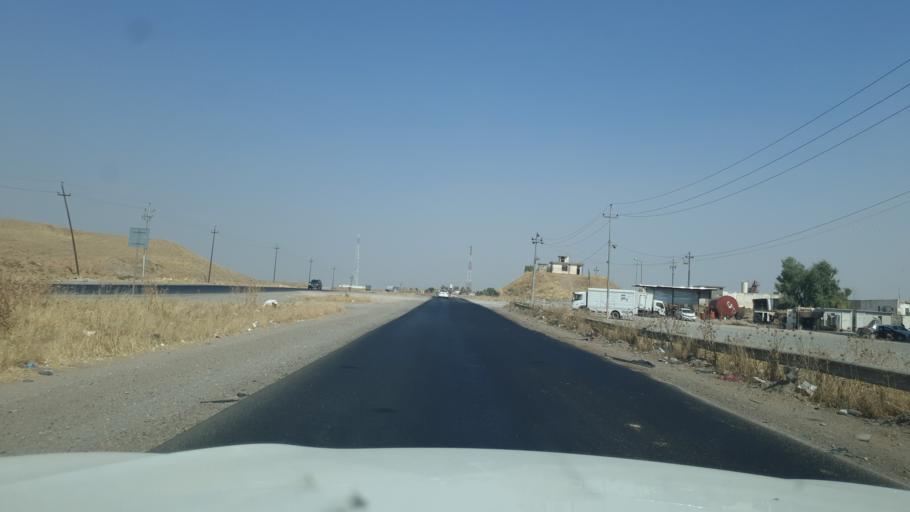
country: IQ
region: Arbil
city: Erbil
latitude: 36.1959
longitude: 43.8977
